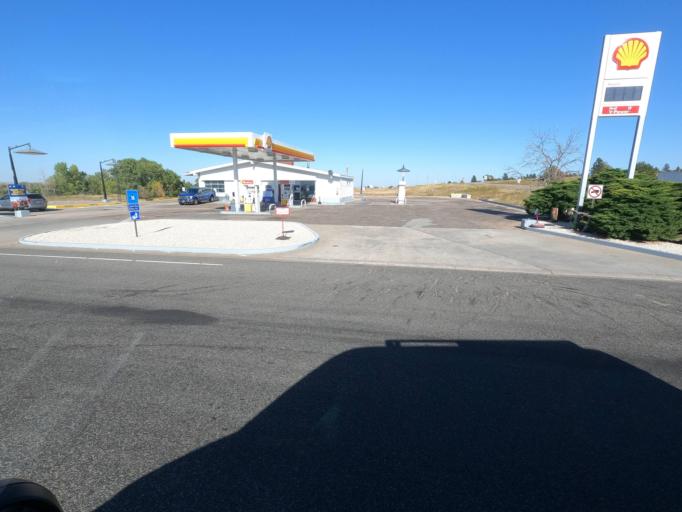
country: US
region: Colorado
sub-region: Sedgwick County
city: Julesburg
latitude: 40.9692
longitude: -102.2481
